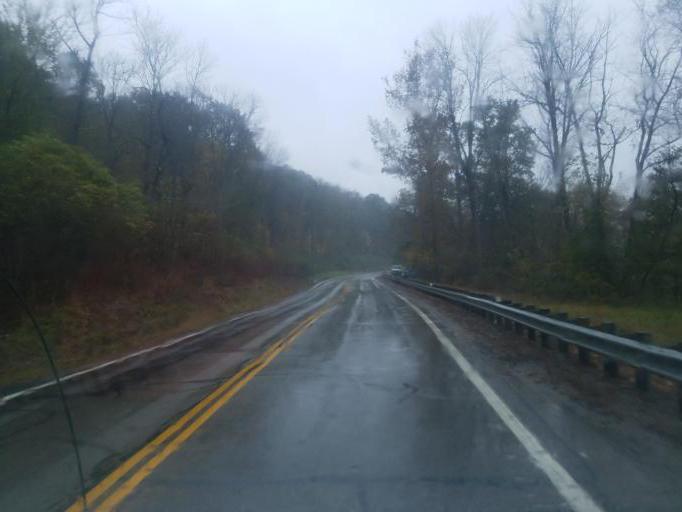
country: US
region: Ohio
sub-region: Morgan County
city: McConnelsville
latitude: 39.7655
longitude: -81.8941
